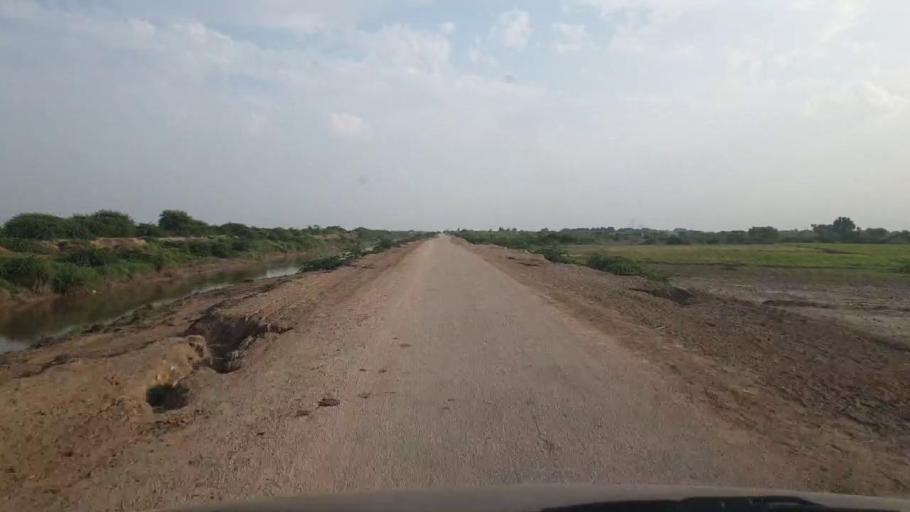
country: PK
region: Sindh
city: Badin
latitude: 24.5380
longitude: 68.6754
